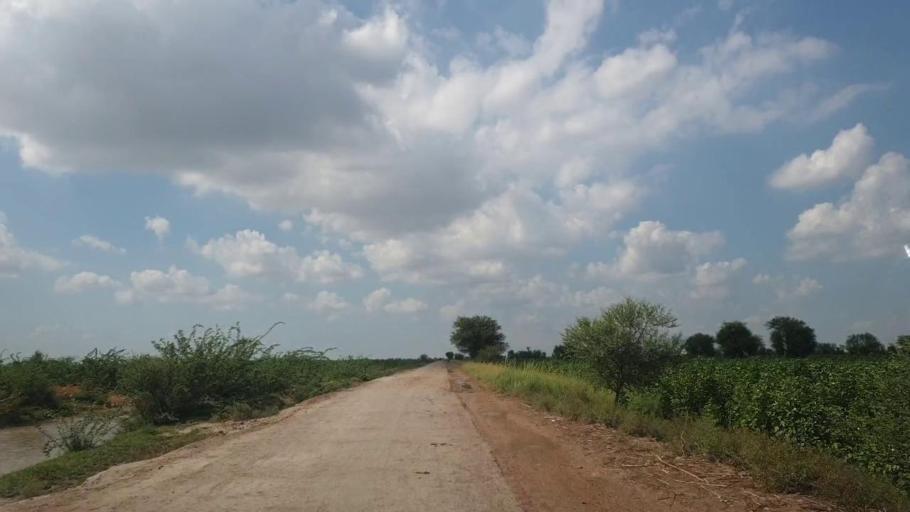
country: PK
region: Sindh
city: Pithoro
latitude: 25.5882
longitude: 69.3590
